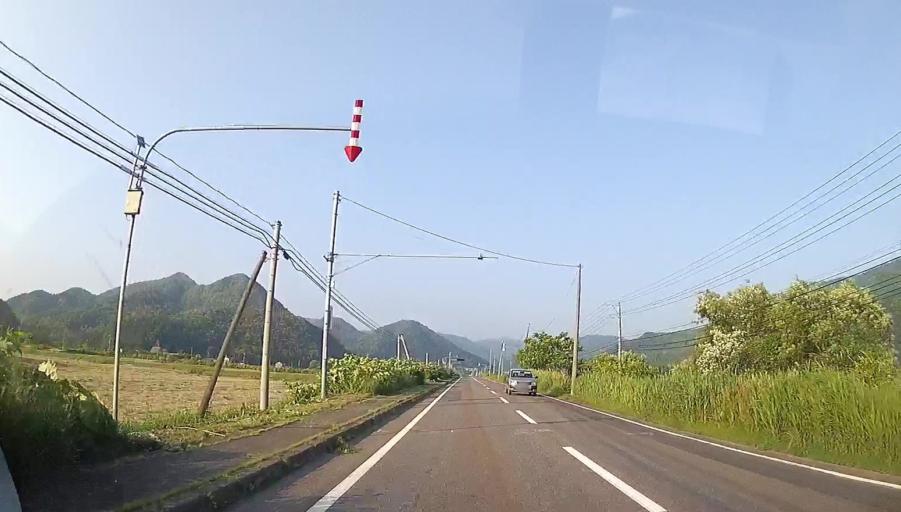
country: JP
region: Hokkaido
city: Shimo-furano
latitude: 42.8826
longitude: 142.4539
